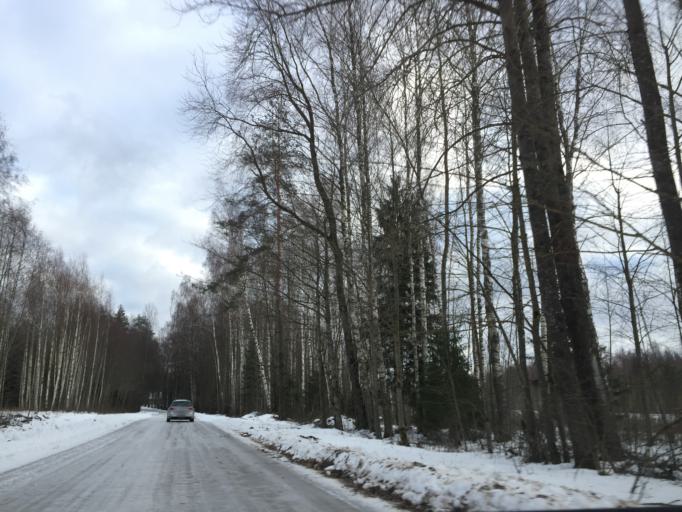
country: LV
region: Lielvarde
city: Lielvarde
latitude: 56.5801
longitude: 24.7739
